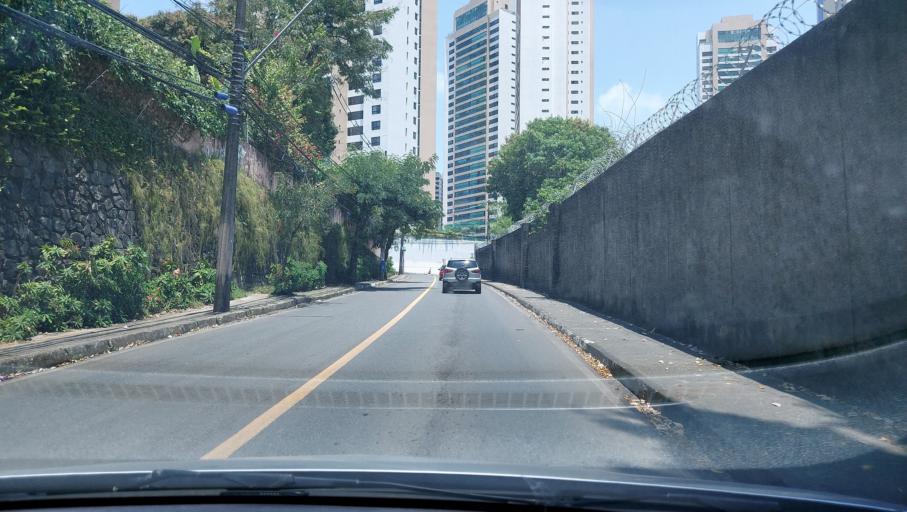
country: BR
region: Bahia
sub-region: Salvador
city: Salvador
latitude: -13.0005
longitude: -38.4854
